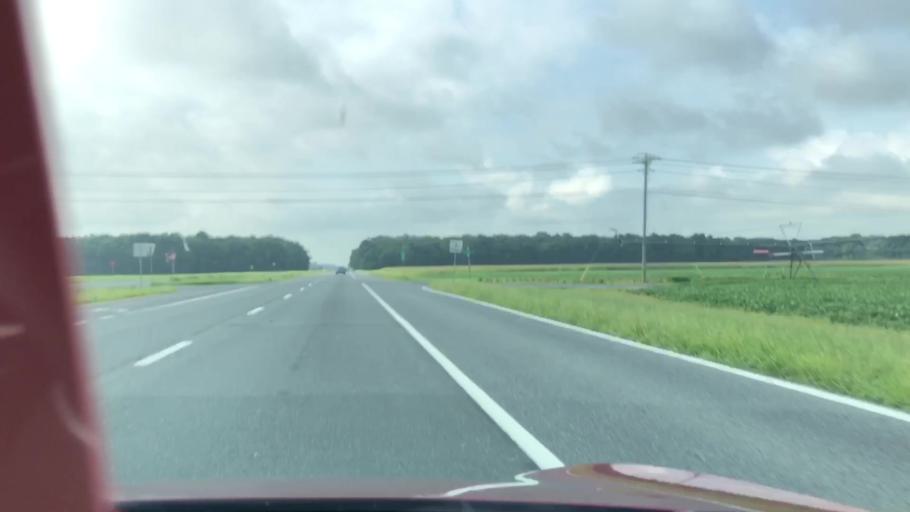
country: US
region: Delaware
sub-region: Sussex County
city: Laurel
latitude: 38.5140
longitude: -75.5572
